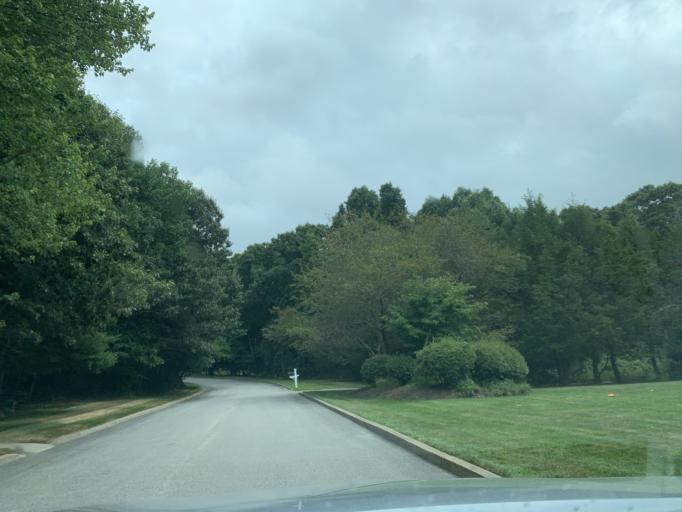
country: US
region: Rhode Island
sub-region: Kent County
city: West Warwick
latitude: 41.6541
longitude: -71.5269
